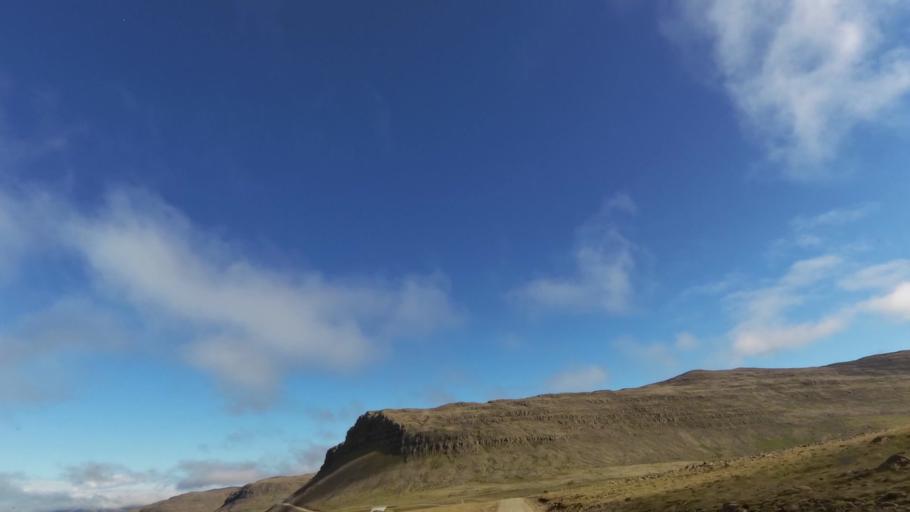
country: IS
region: West
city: Olafsvik
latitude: 65.5740
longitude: -24.0650
